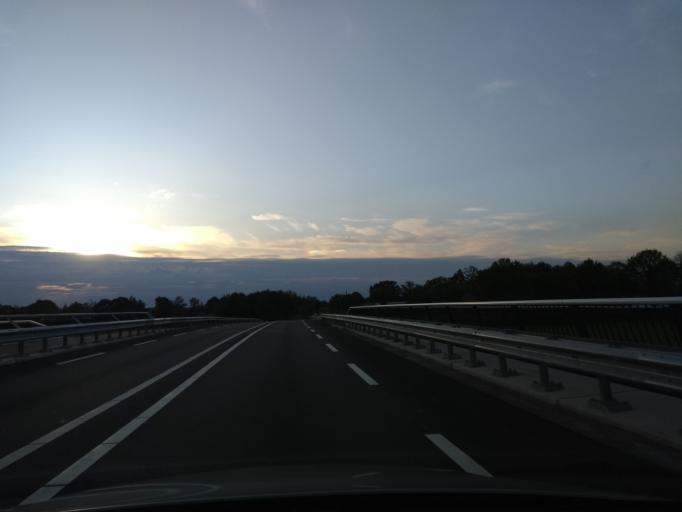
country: NL
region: Overijssel
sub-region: Gemeente Haaksbergen
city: Haaksbergen
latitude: 52.1704
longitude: 6.7126
